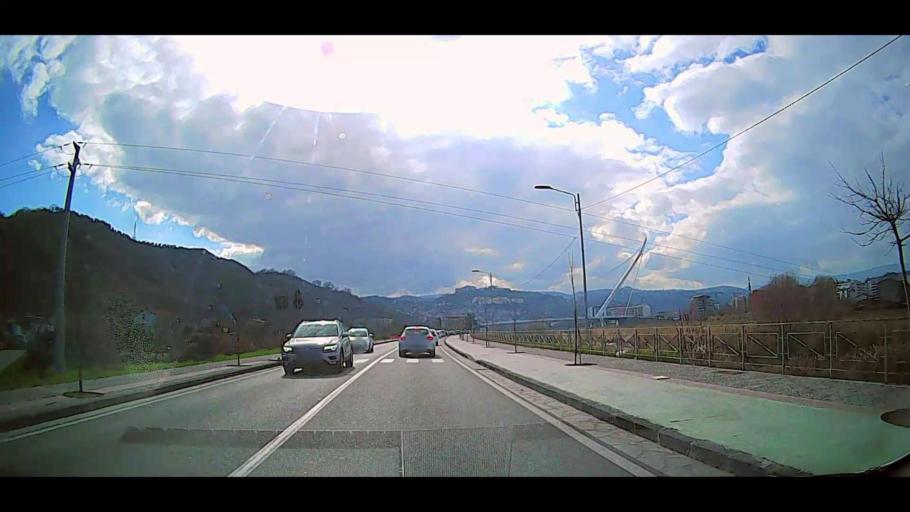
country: IT
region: Calabria
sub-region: Provincia di Cosenza
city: Cosenza
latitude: 39.3030
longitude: 16.2630
